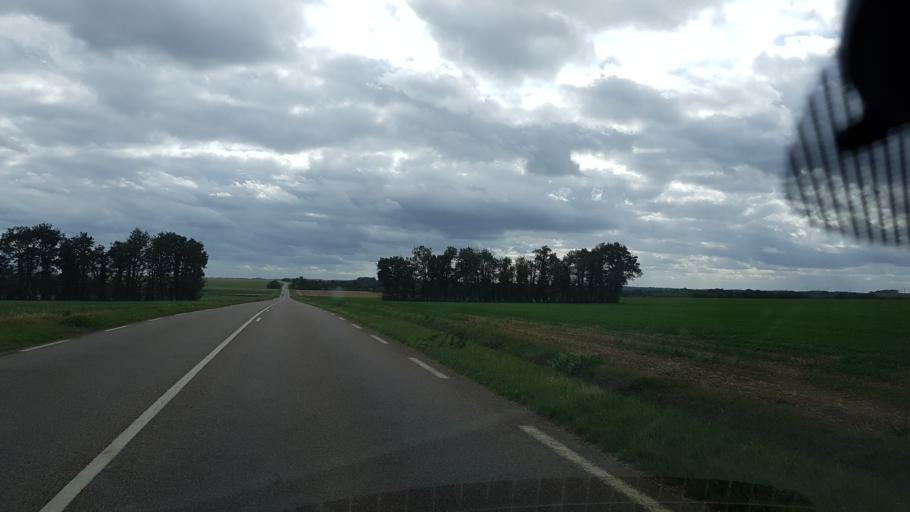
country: FR
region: Ile-de-France
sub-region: Departement de l'Essonne
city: Saclas
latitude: 48.3838
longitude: 2.1689
